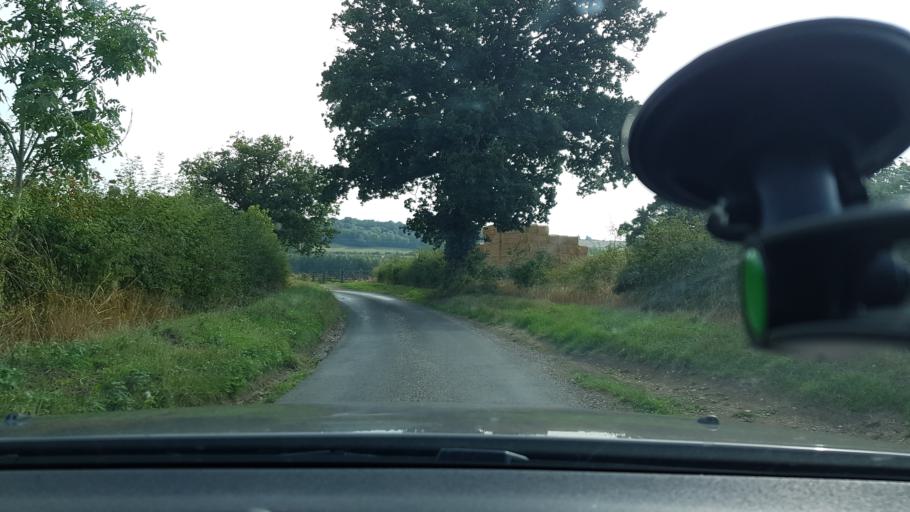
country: GB
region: England
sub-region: Wiltshire
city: Ramsbury
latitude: 51.4475
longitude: -1.5789
